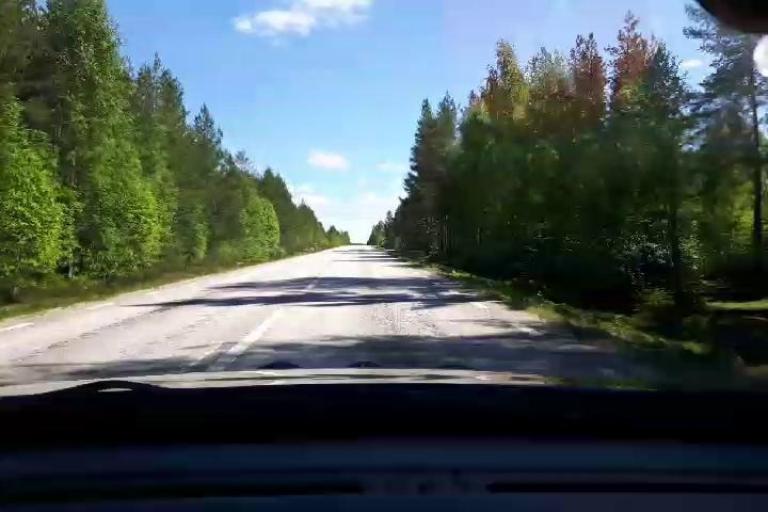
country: SE
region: Gaevleborg
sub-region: Ljusdals Kommun
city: Farila
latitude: 61.9909
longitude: 15.2660
